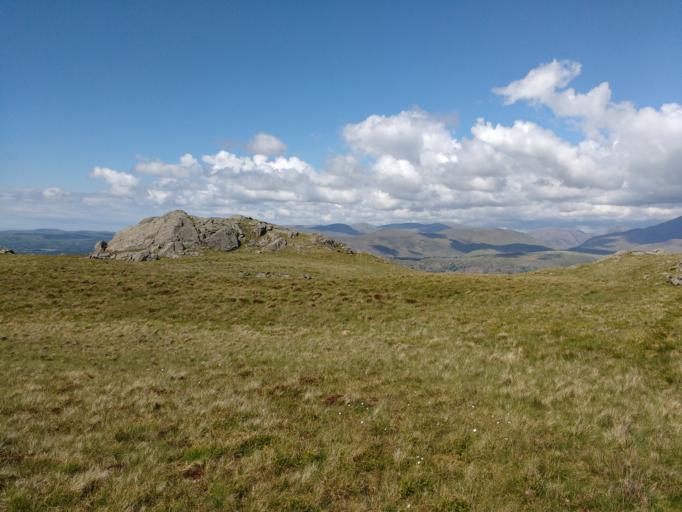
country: GB
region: England
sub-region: Cumbria
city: Millom
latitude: 54.3500
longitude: -3.3088
